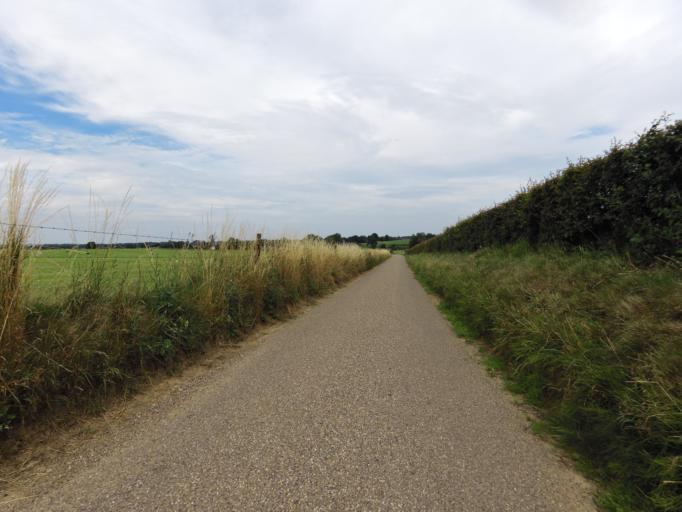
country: NL
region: Limburg
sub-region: Gemeente Simpelveld
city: Simpelveld
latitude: 50.8080
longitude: 6.0010
